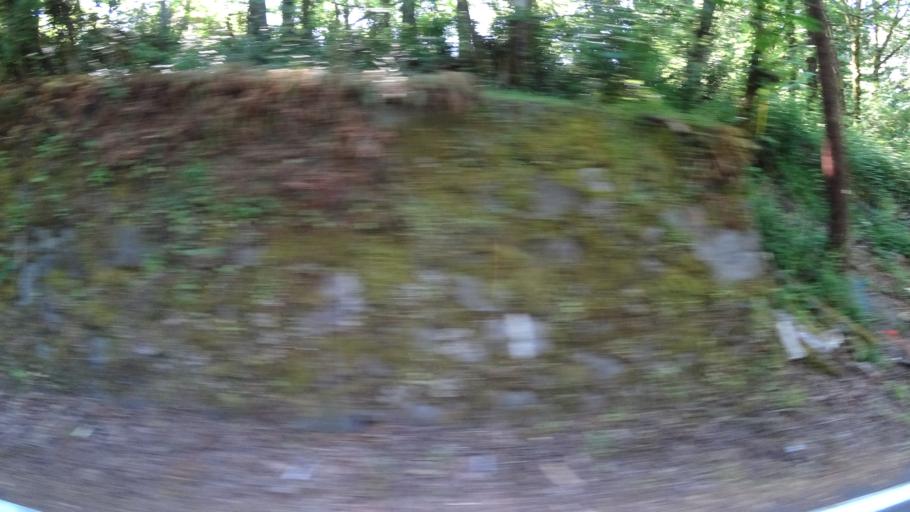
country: US
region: Oregon
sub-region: Clackamas County
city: Happy Valley
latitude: 45.4678
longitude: -122.5284
